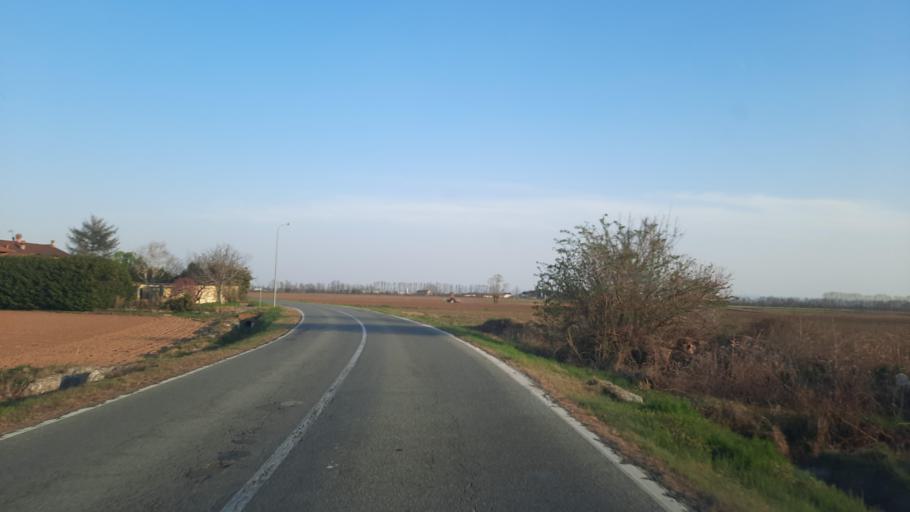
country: IT
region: Piedmont
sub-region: Provincia di Vercelli
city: Livorno Ferraris
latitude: 45.3204
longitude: 8.0824
